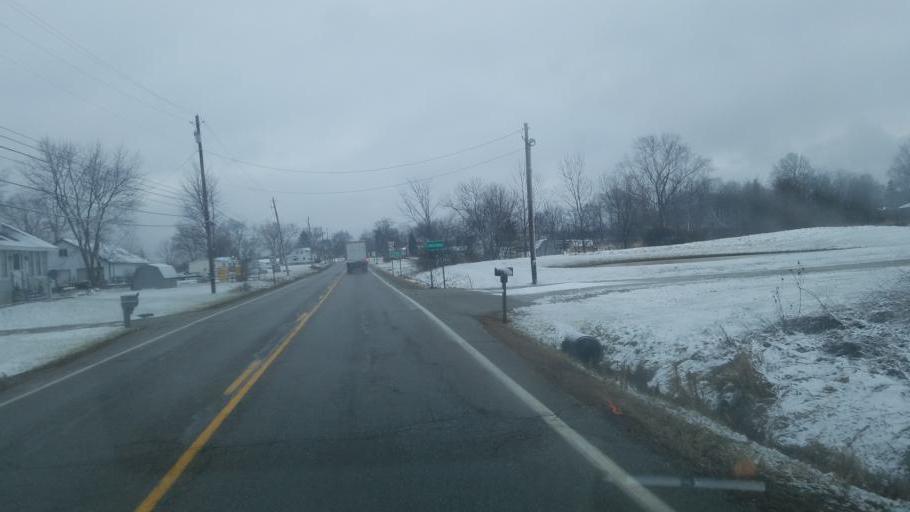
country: US
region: Ohio
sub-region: Portage County
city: Garrettsville
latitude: 41.2358
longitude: -81.1377
